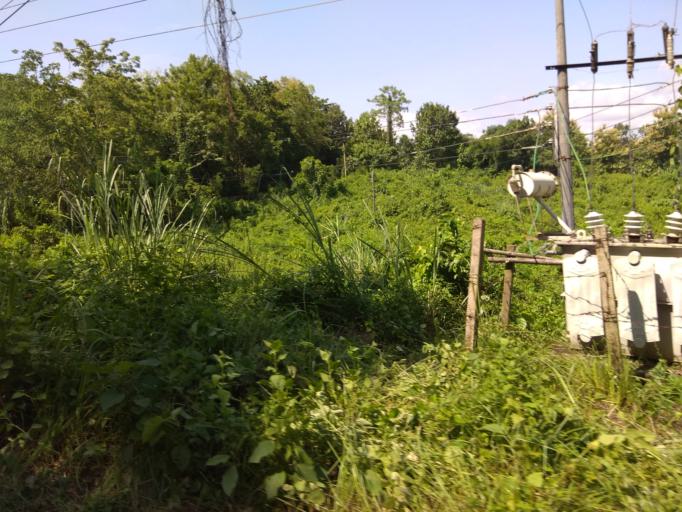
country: BD
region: Chittagong
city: Khagrachhari
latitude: 23.0292
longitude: 92.0140
